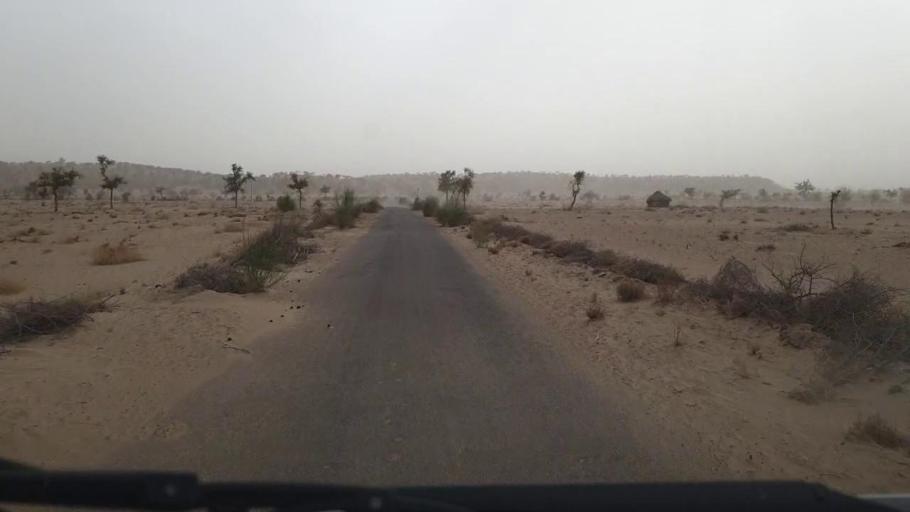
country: PK
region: Sindh
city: Islamkot
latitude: 25.0670
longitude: 70.5524
